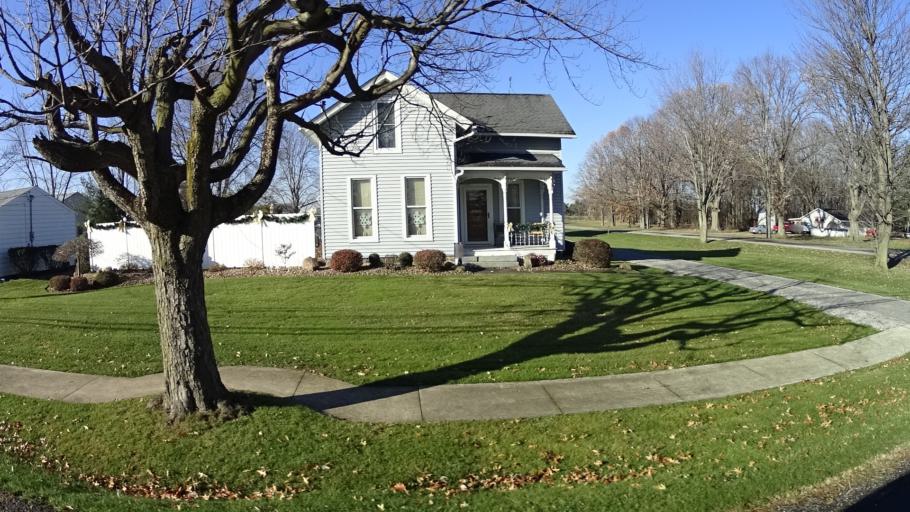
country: US
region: Ohio
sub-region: Lorain County
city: Lagrange
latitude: 41.2323
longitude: -82.1199
